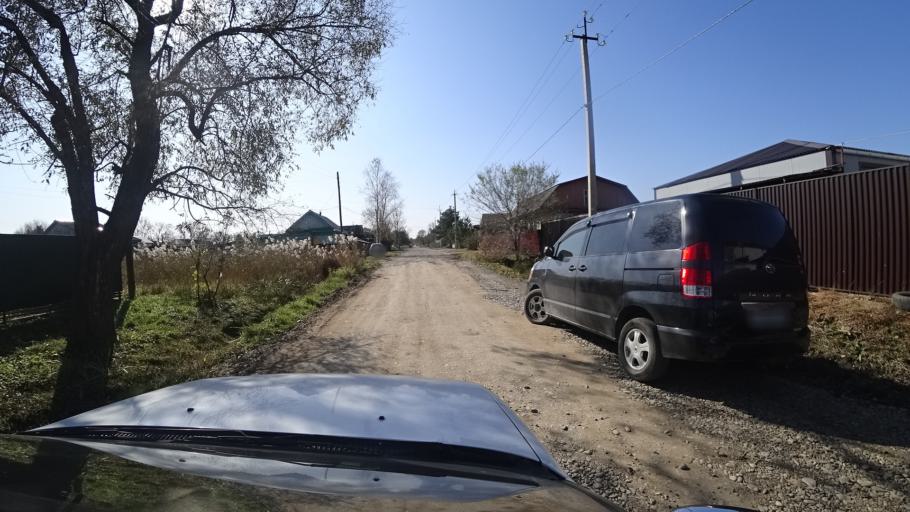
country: RU
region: Primorskiy
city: Dal'nerechensk
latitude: 45.9273
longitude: 133.7415
